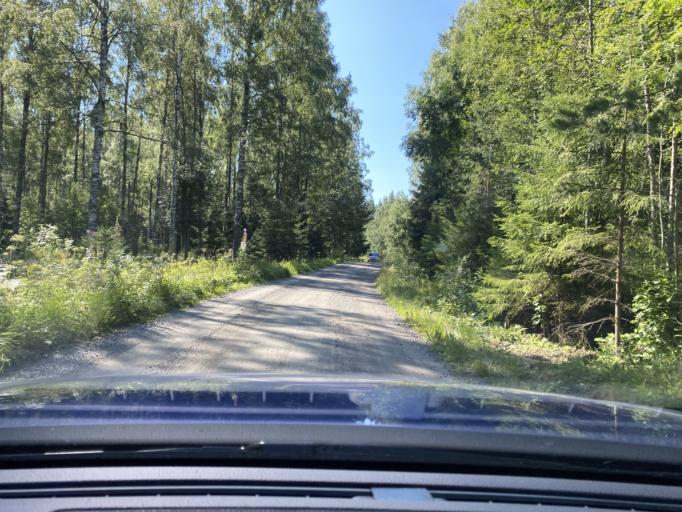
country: FI
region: Central Finland
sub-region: Jaemsae
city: Jaemsae
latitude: 61.8613
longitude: 25.3960
